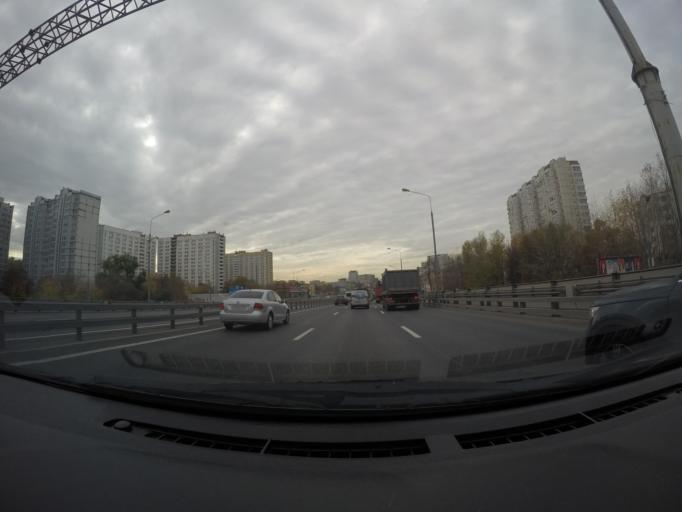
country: RU
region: Moscow
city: Yaroslavskiy
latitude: 55.8692
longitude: 37.7096
